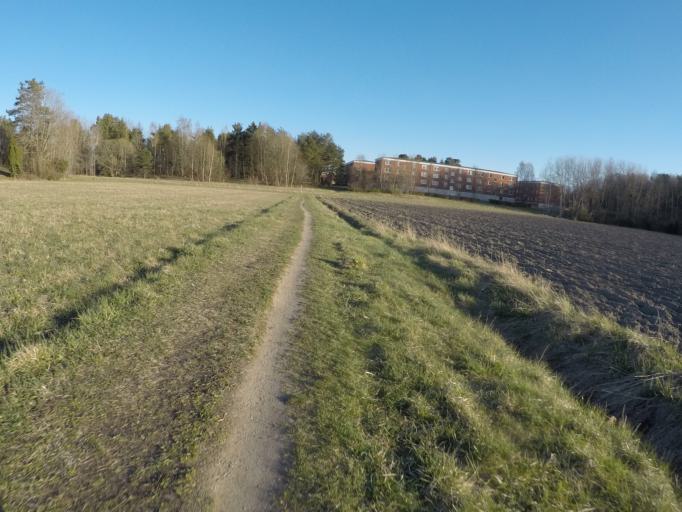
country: SE
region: Soedermanland
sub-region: Eskilstuna Kommun
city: Eskilstuna
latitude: 59.3962
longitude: 16.5297
